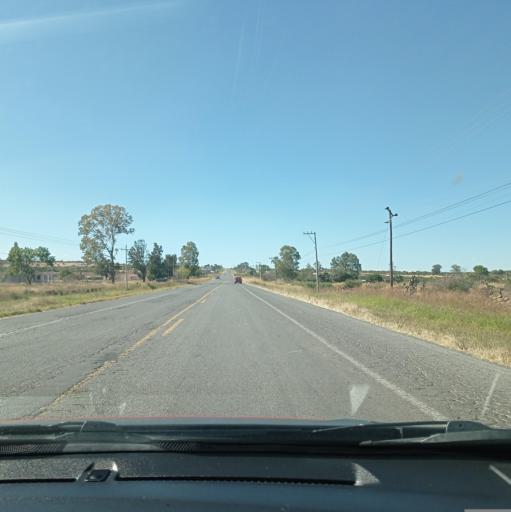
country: MX
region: Jalisco
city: San Miguel el Alto
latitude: 21.0099
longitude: -102.3026
